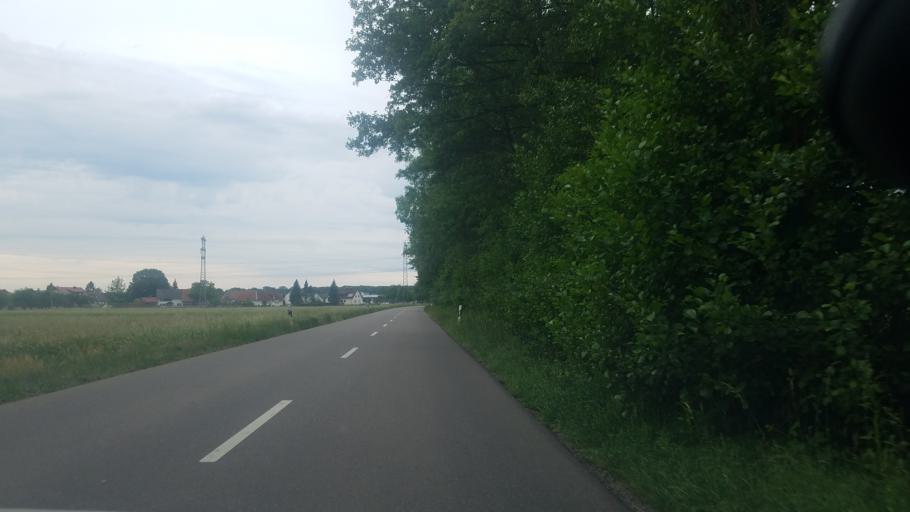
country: DE
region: Baden-Wuerttemberg
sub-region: Freiburg Region
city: Achern
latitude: 48.6458
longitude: 8.0519
